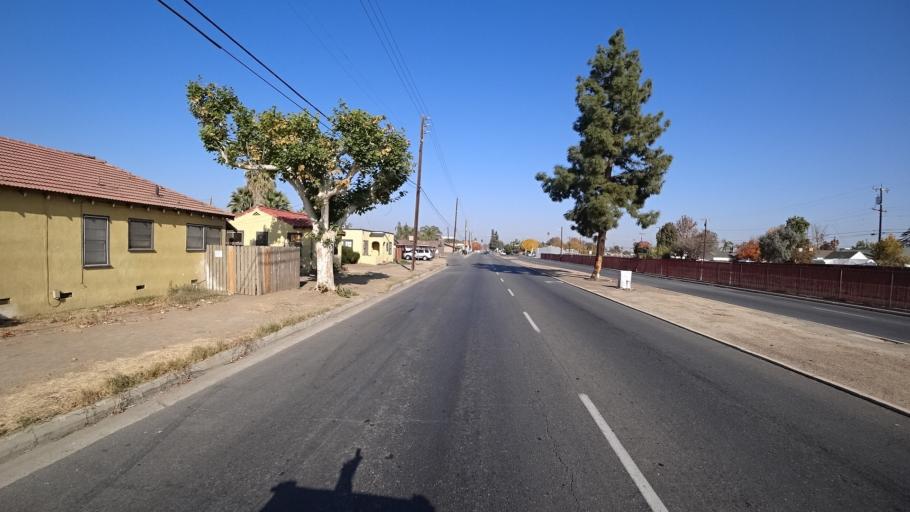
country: US
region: California
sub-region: Kern County
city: Bakersfield
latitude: 35.3450
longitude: -119.0213
